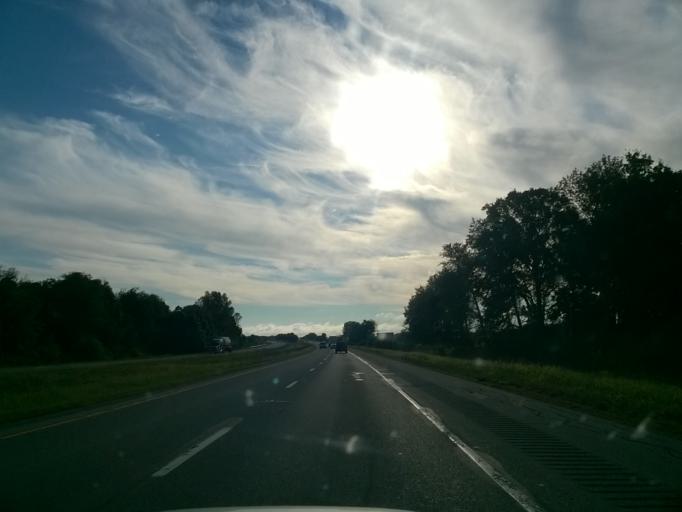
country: US
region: Indiana
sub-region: Spencer County
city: Dale
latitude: 38.1965
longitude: -87.0196
